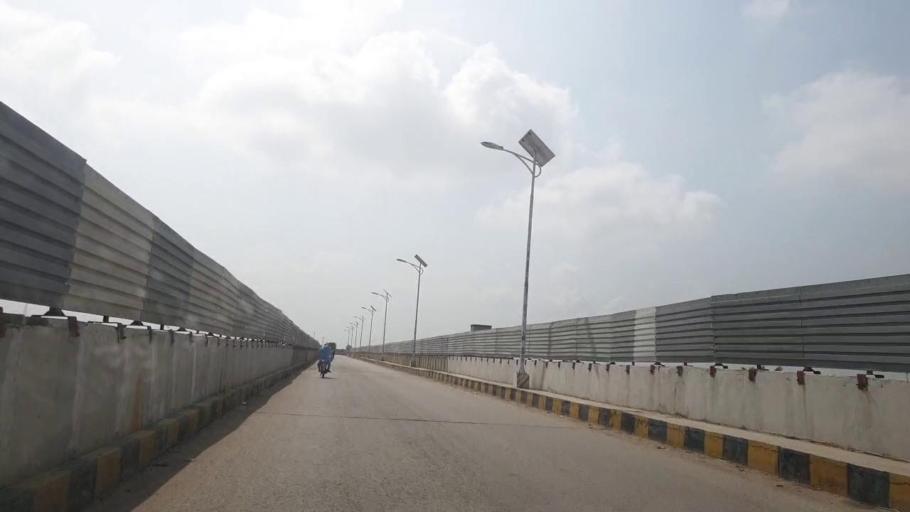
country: PK
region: Sindh
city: Khairpur
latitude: 27.5286
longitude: 68.7415
